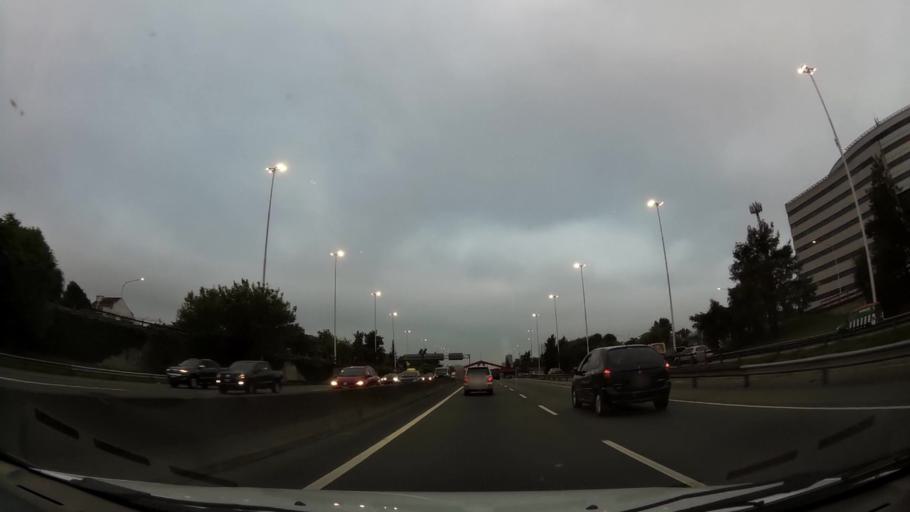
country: AR
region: Buenos Aires
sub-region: Partido de Vicente Lopez
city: Olivos
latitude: -34.5447
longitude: -58.4888
